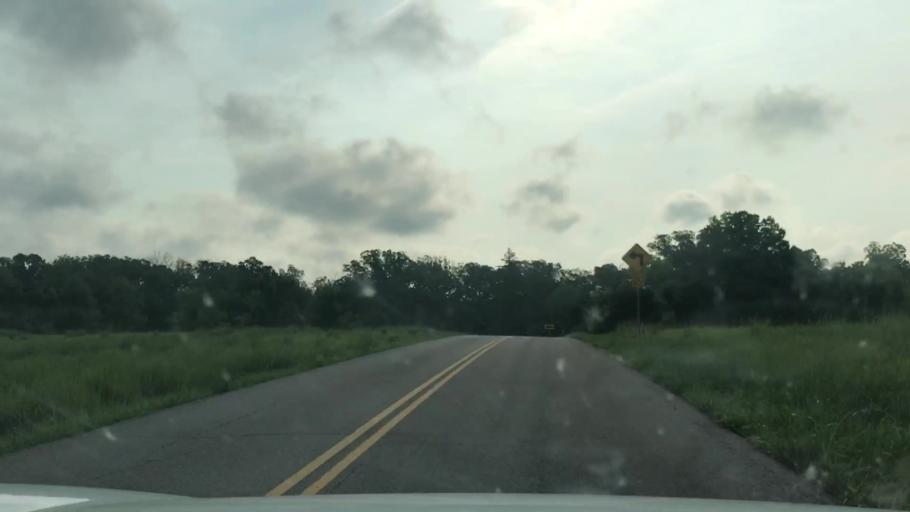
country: US
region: Missouri
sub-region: Saint Charles County
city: Cottleville
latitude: 38.7045
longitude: -90.6440
